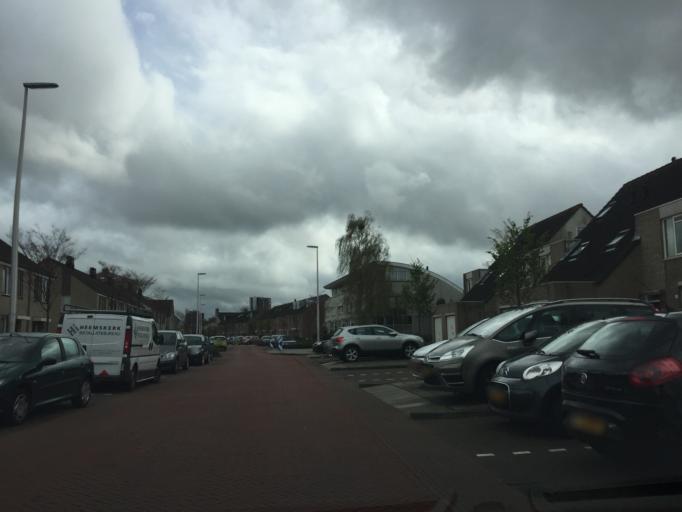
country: NL
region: South Holland
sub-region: Gemeente Leiderdorp
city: Leiderdorp
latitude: 52.1702
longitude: 4.5287
